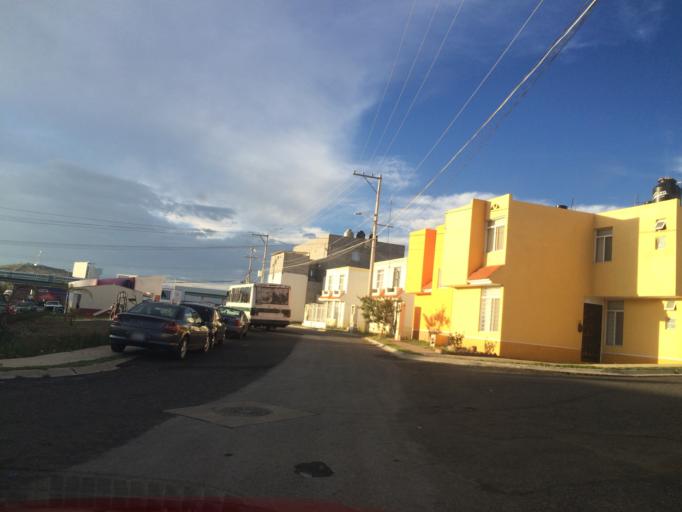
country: MX
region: Zacatecas
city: Zacatecas
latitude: 22.7690
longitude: -102.6116
